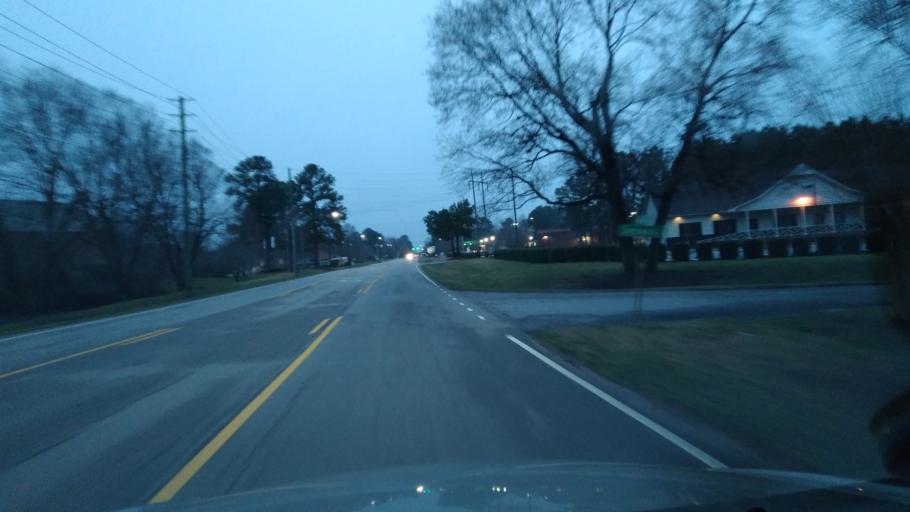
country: US
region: North Carolina
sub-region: Wake County
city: Garner
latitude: 35.7023
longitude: -78.6124
